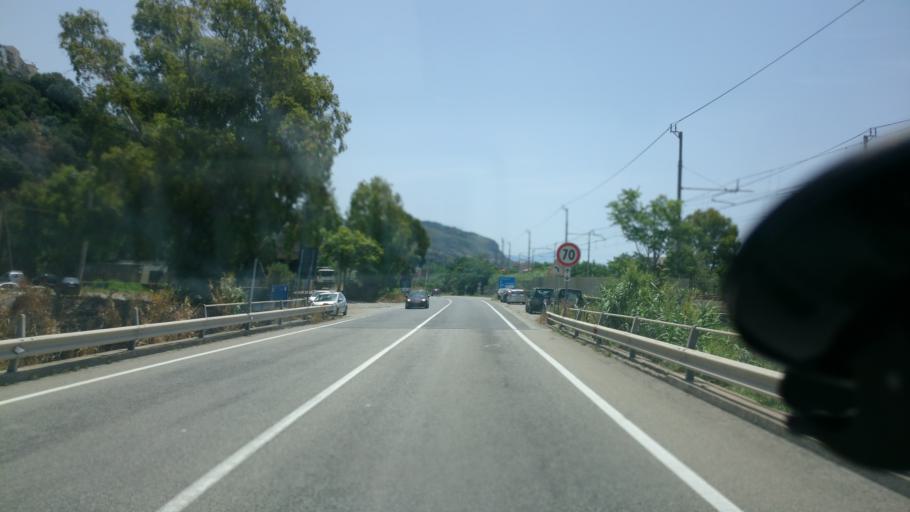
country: IT
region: Calabria
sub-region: Provincia di Cosenza
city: Cetraro Marina
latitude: 39.5186
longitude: 15.9338
